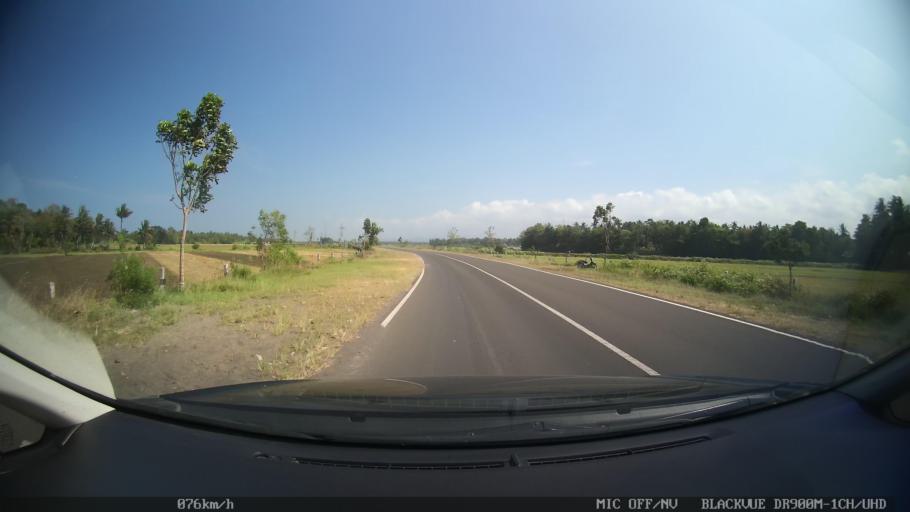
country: ID
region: Daerah Istimewa Yogyakarta
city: Srandakan
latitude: -7.9594
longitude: 110.2024
